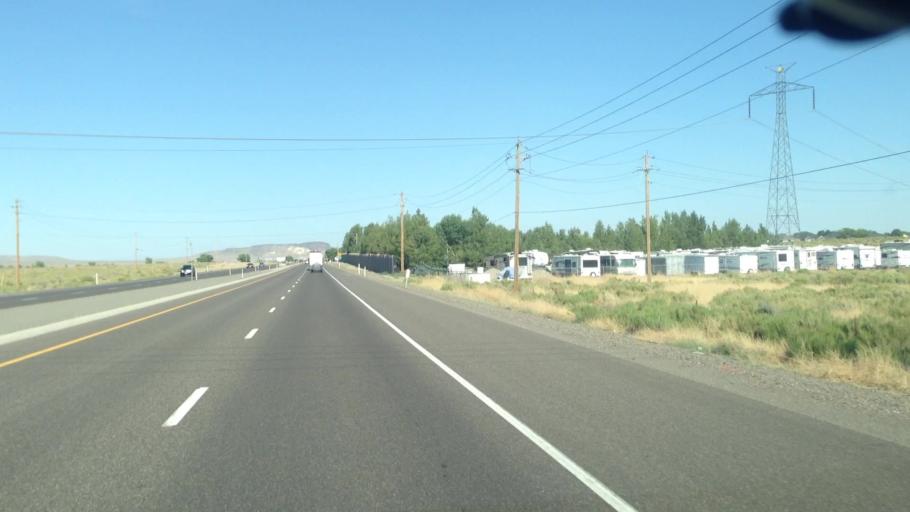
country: US
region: Nevada
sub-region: Lyon County
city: Fernley
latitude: 39.5937
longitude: -119.1629
